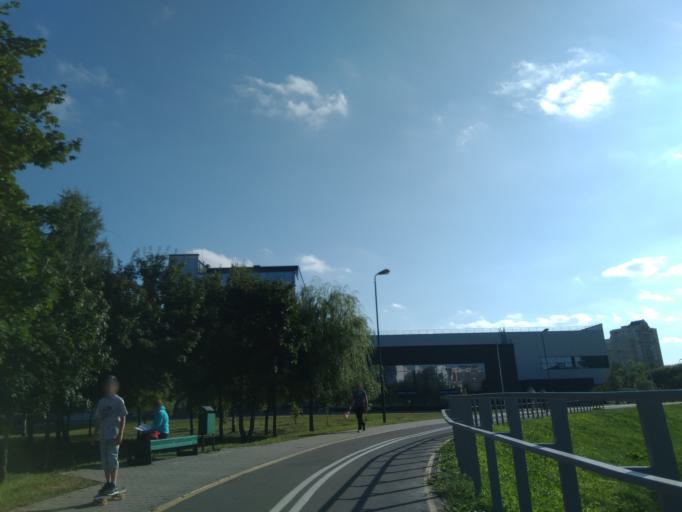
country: BY
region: Minsk
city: Minsk
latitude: 53.8686
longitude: 27.5911
